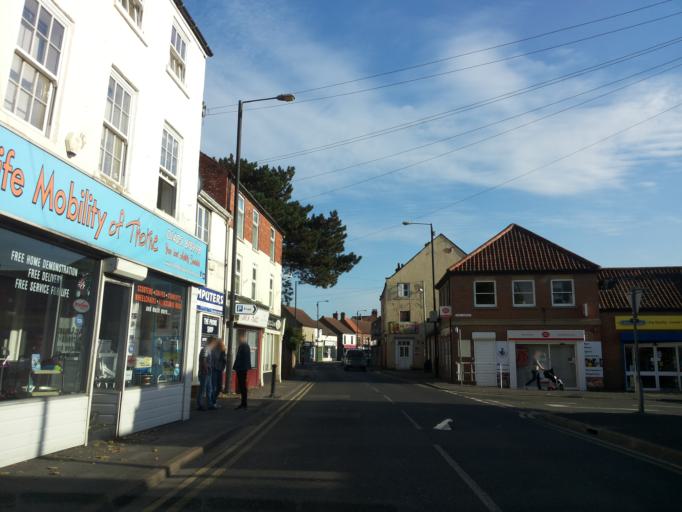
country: GB
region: England
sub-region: Doncaster
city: Hatfield
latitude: 53.6121
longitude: -0.9629
